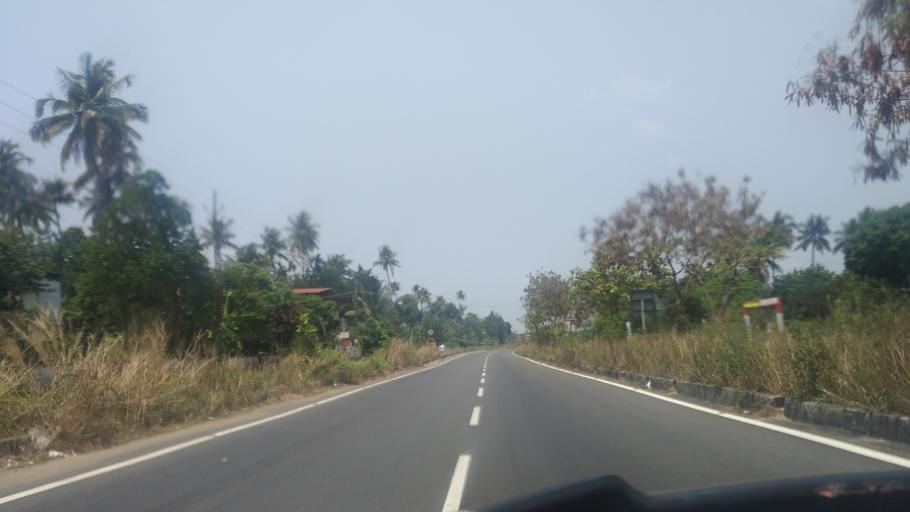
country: IN
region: Kerala
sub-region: Thrissur District
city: Kodungallur
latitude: 10.2268
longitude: 76.1957
